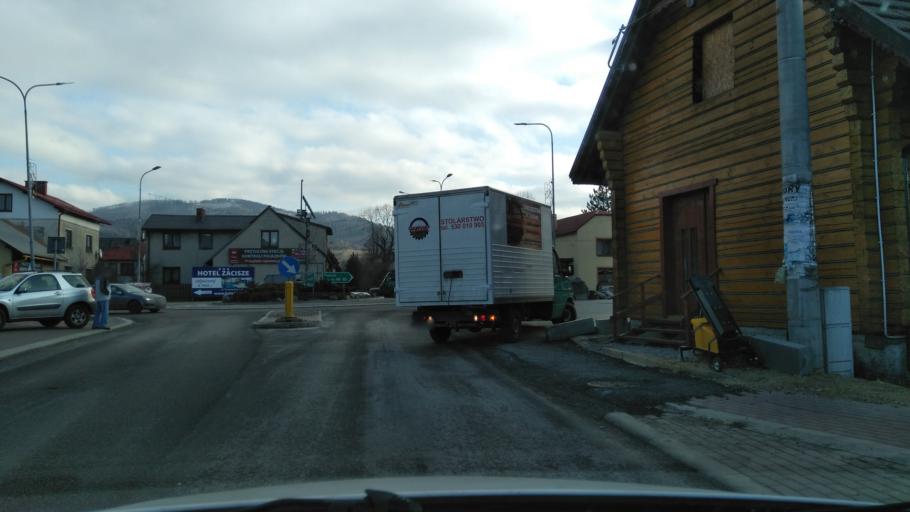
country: PL
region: Silesian Voivodeship
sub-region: Powiat zywiecki
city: Milowka
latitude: 49.5594
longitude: 19.0862
